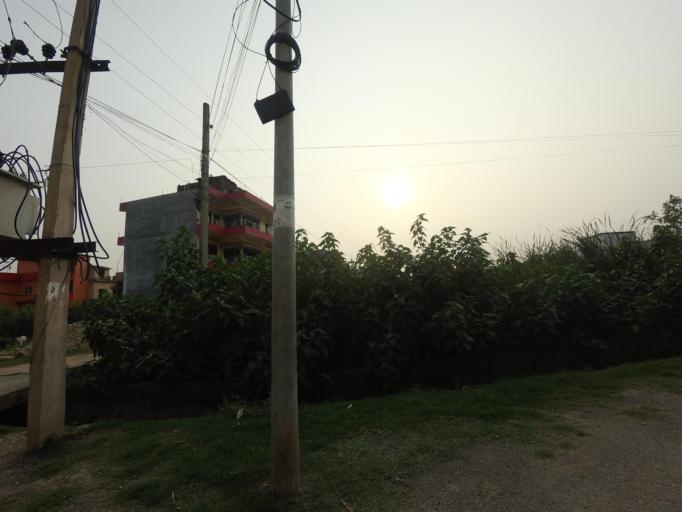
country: NP
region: Western Region
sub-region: Lumbini Zone
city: Bhairahawa
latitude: 27.5093
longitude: 83.4469
